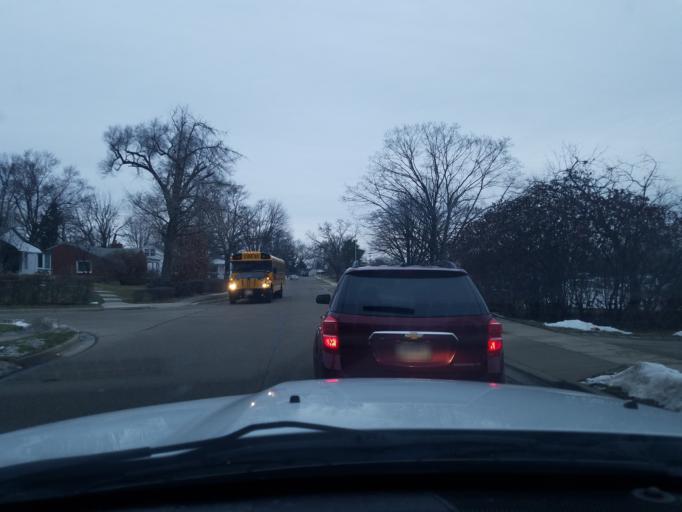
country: US
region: Ohio
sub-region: Montgomery County
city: Kettering
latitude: 39.7051
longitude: -84.1501
